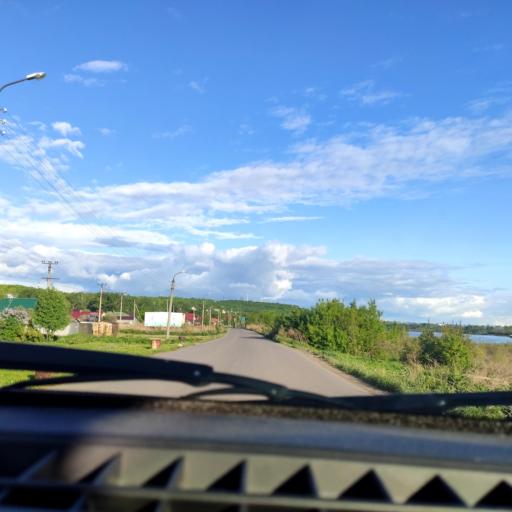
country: RU
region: Bashkortostan
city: Blagoveshchensk
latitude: 54.8946
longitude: 56.0274
